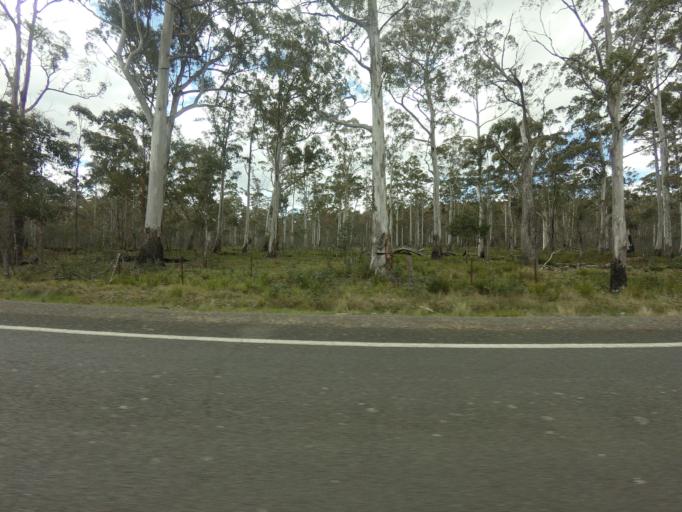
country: AU
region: Tasmania
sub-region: Northern Midlands
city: Evandale
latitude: -41.9888
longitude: 147.7060
